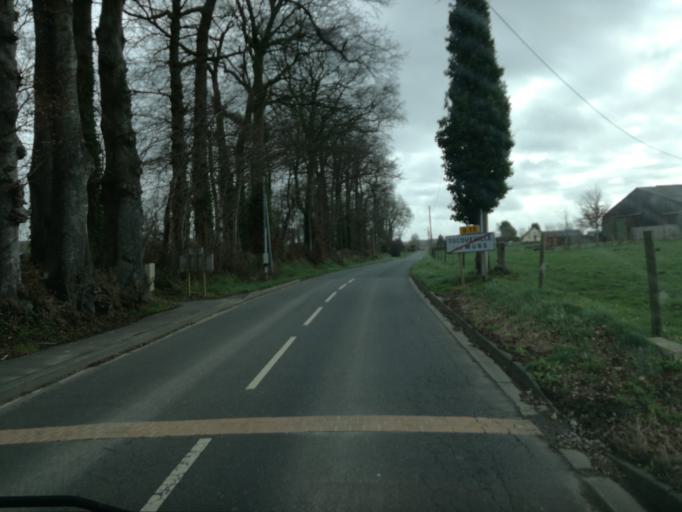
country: FR
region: Haute-Normandie
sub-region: Departement de la Seine-Maritime
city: Yebleron
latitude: 49.6645
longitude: 0.5054
